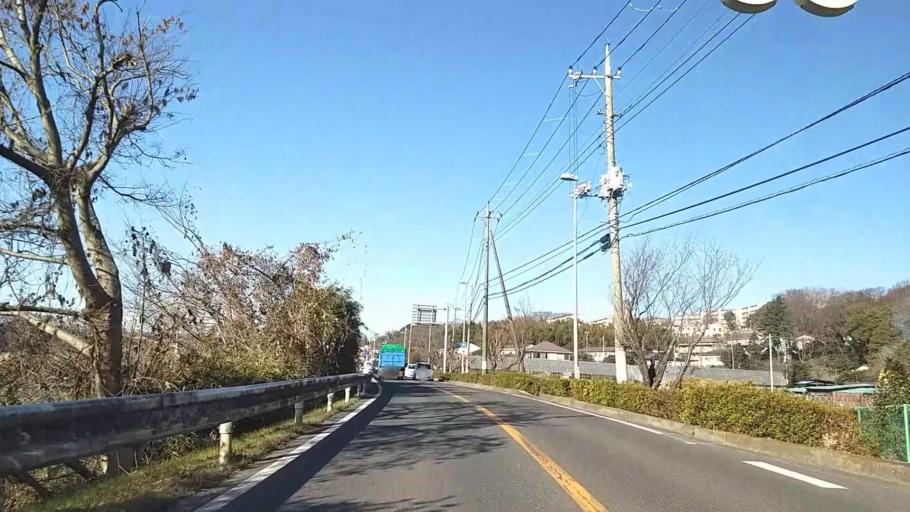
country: JP
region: Kanagawa
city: Hadano
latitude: 35.3565
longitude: 139.2691
